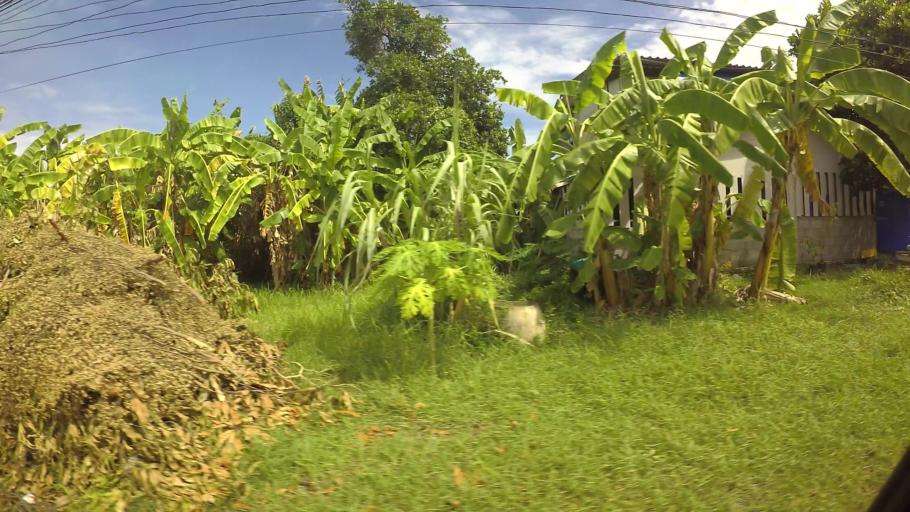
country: TH
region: Chon Buri
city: Sattahip
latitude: 12.6650
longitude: 100.9150
